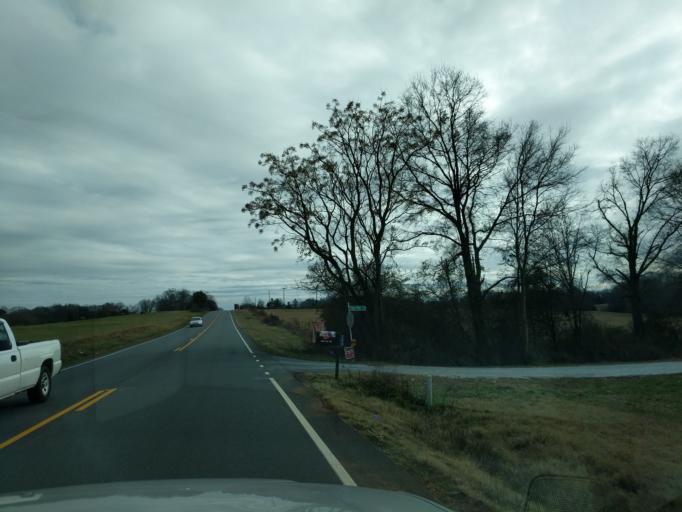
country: US
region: South Carolina
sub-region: Oconee County
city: Utica
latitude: 34.5796
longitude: -82.9144
